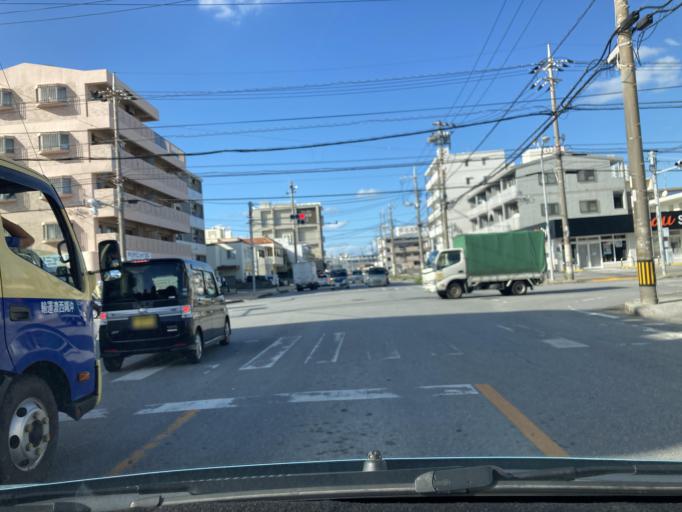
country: JP
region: Okinawa
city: Okinawa
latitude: 26.3422
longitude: 127.8240
